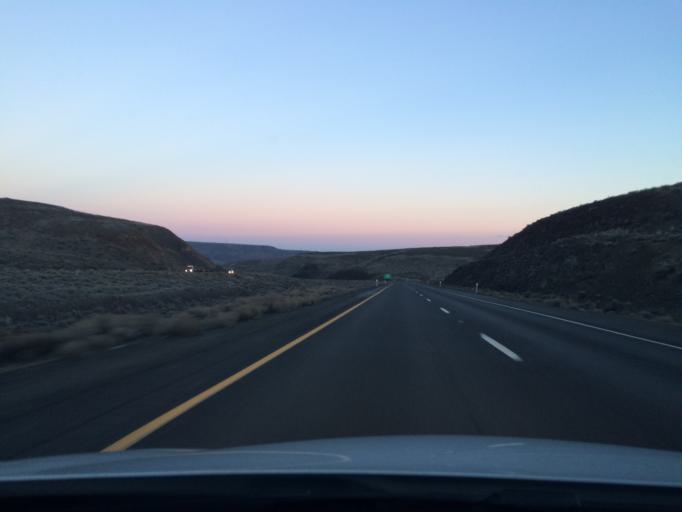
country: US
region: Washington
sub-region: Grant County
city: Mattawa
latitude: 46.9382
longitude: -120.0218
